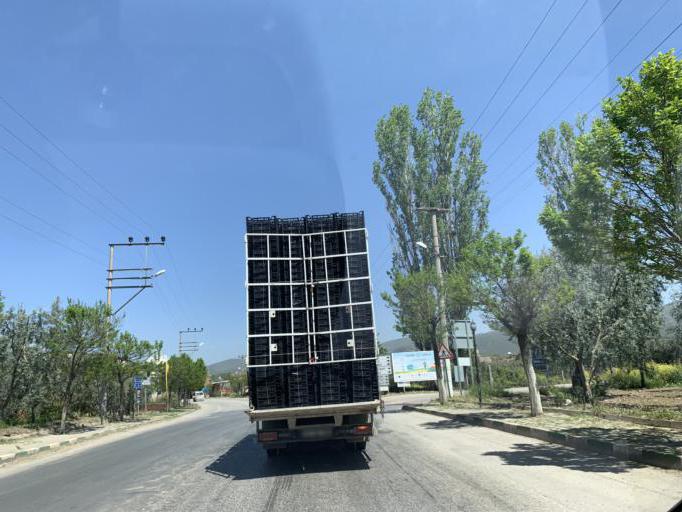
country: TR
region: Bursa
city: Iznik
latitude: 40.4216
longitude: 29.7194
